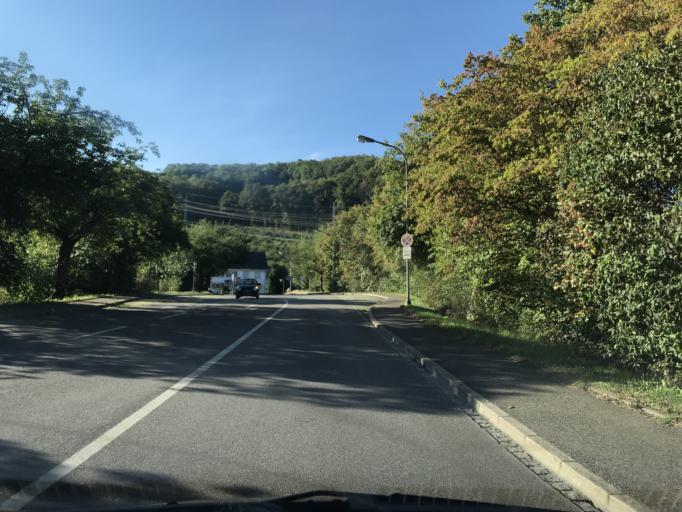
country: DE
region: Baden-Wuerttemberg
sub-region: Freiburg Region
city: Loerrach
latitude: 47.6311
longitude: 7.6830
